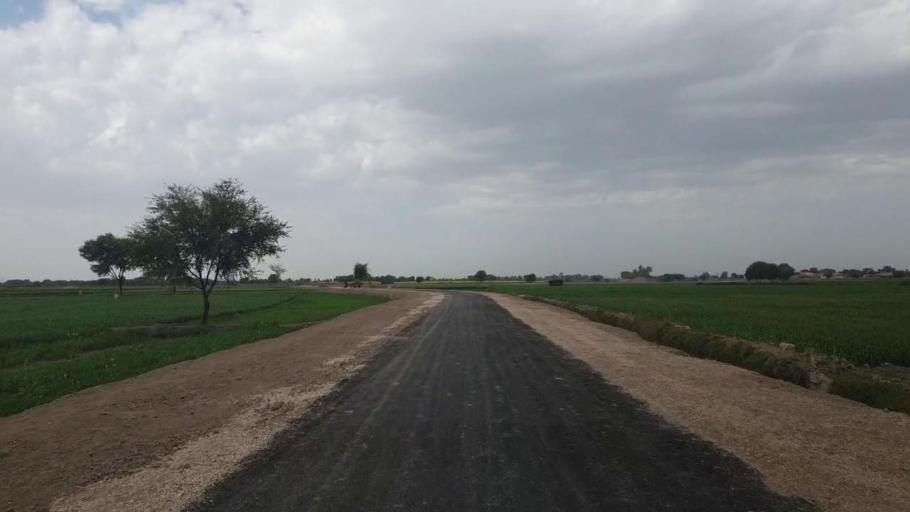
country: PK
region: Sindh
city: Hala
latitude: 25.9740
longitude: 68.4020
